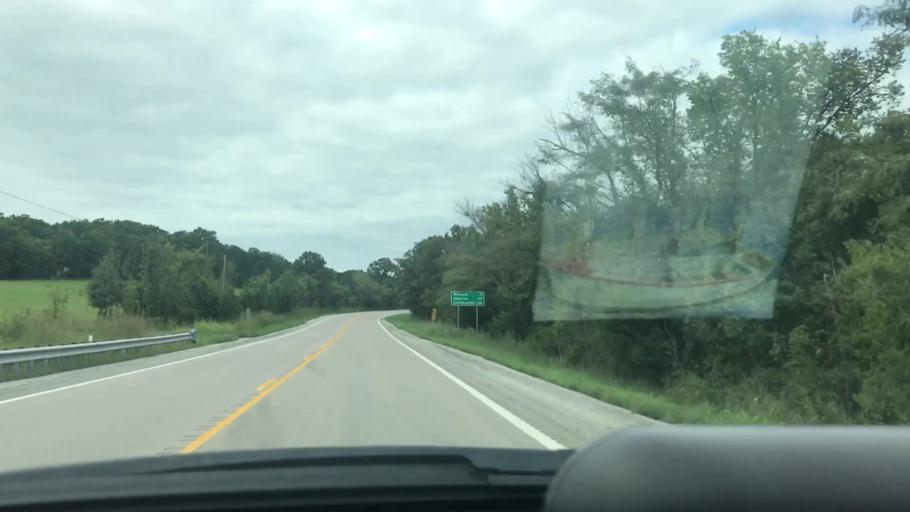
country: US
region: Missouri
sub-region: Benton County
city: Warsaw
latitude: 38.1237
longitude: -93.2792
